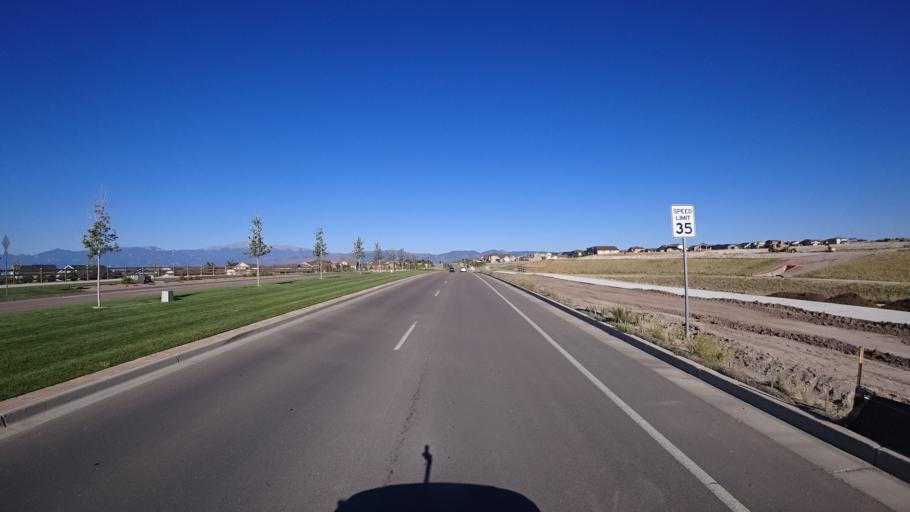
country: US
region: Colorado
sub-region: El Paso County
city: Black Forest
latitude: 38.9709
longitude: -104.7256
